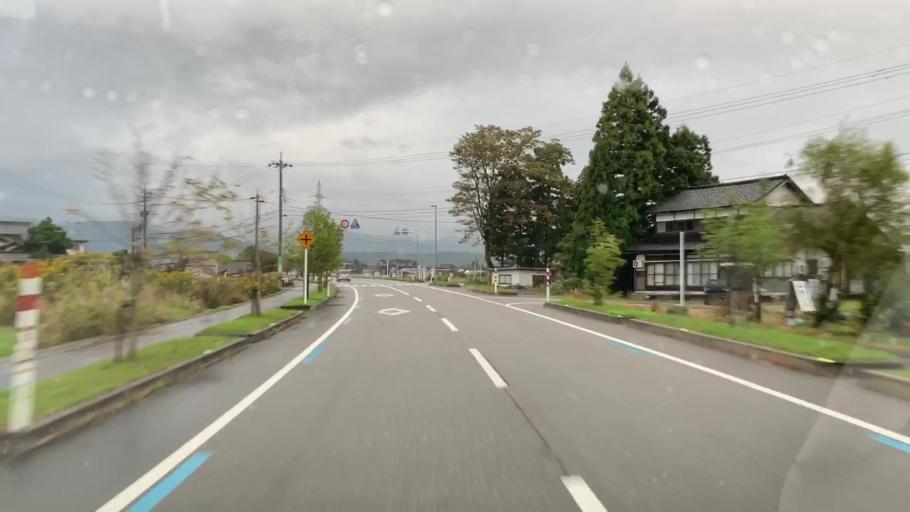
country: JP
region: Toyama
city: Kamiichi
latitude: 36.6133
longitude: 137.3248
